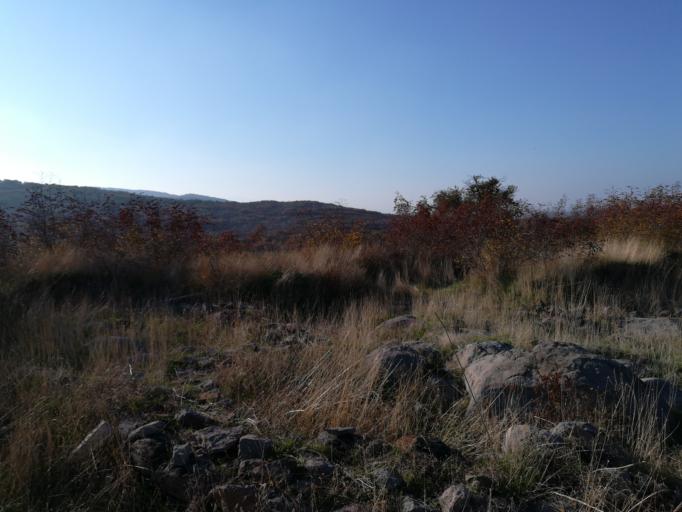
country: BG
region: Khaskovo
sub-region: Obshtina Mineralni Bani
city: Mineralni Bani
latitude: 41.9797
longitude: 25.2382
